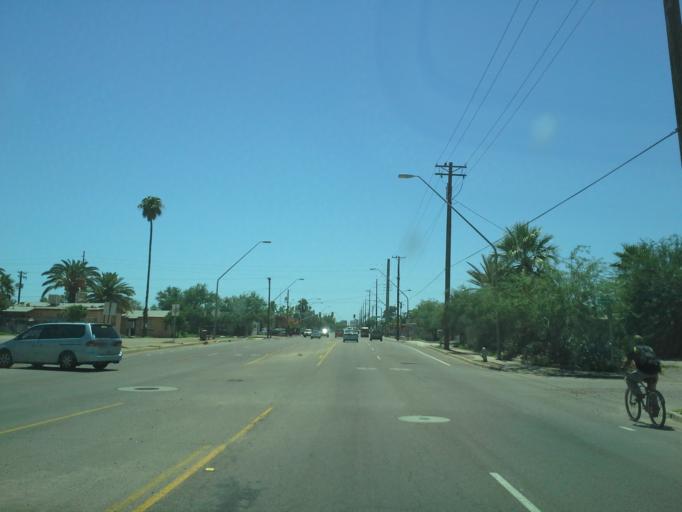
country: US
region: Arizona
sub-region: Pima County
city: Flowing Wells
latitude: 32.2667
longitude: -110.9720
